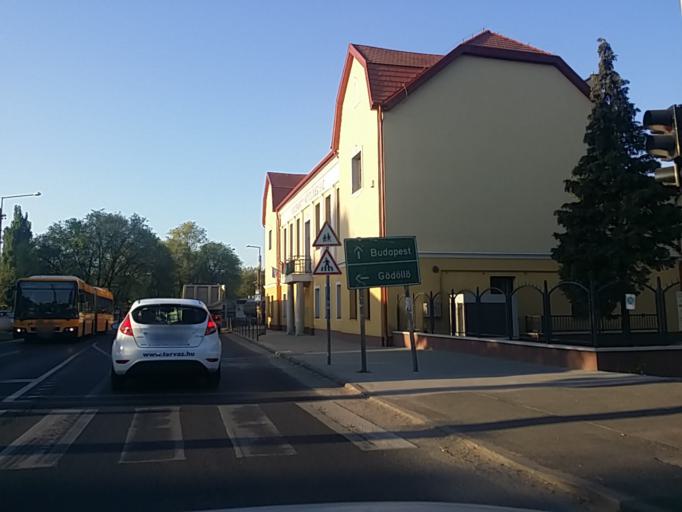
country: HU
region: Pest
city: Fot
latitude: 47.6078
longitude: 19.1970
